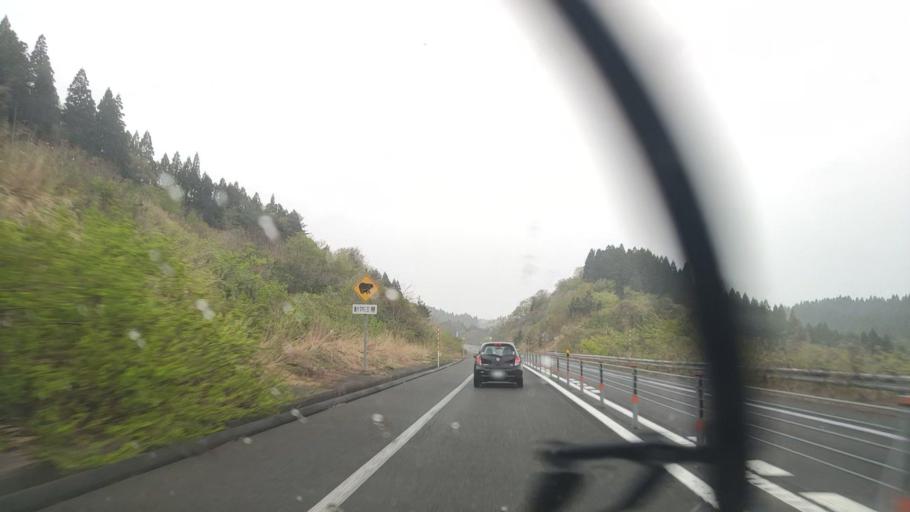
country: JP
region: Akita
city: Noshiromachi
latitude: 40.2007
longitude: 140.1379
